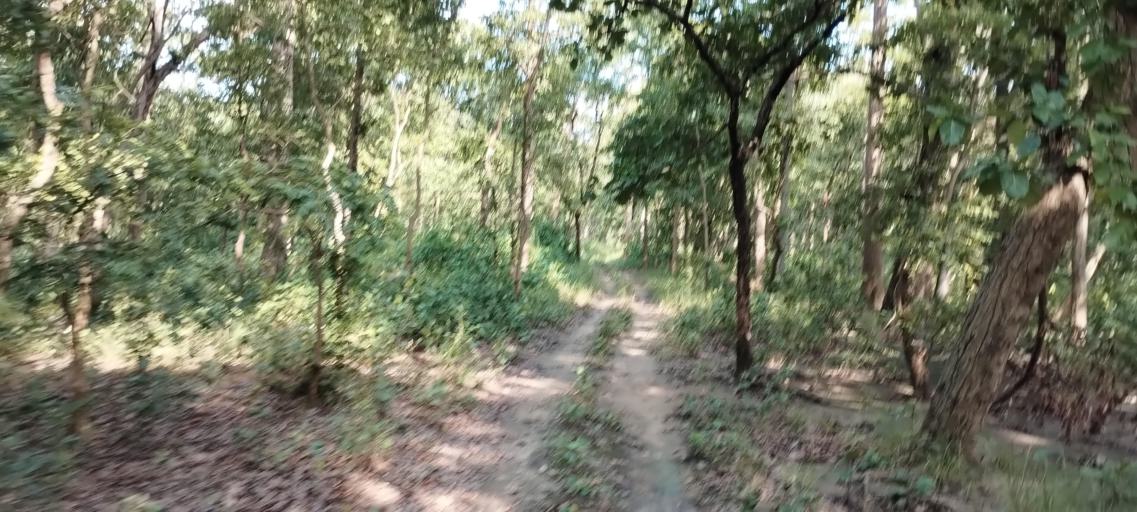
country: NP
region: Far Western
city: Tikapur
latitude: 28.5564
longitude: 81.2663
